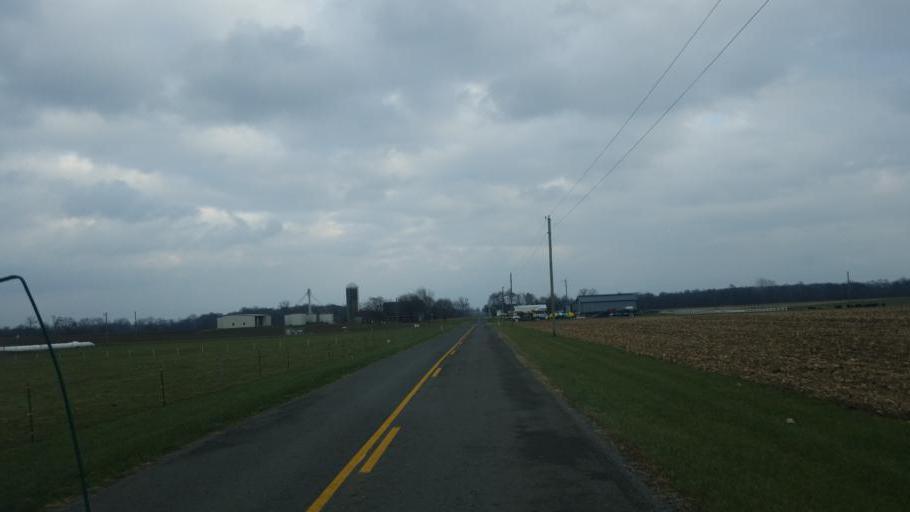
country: US
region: Ohio
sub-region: Mercer County
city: Fort Recovery
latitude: 40.5090
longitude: -84.7532
